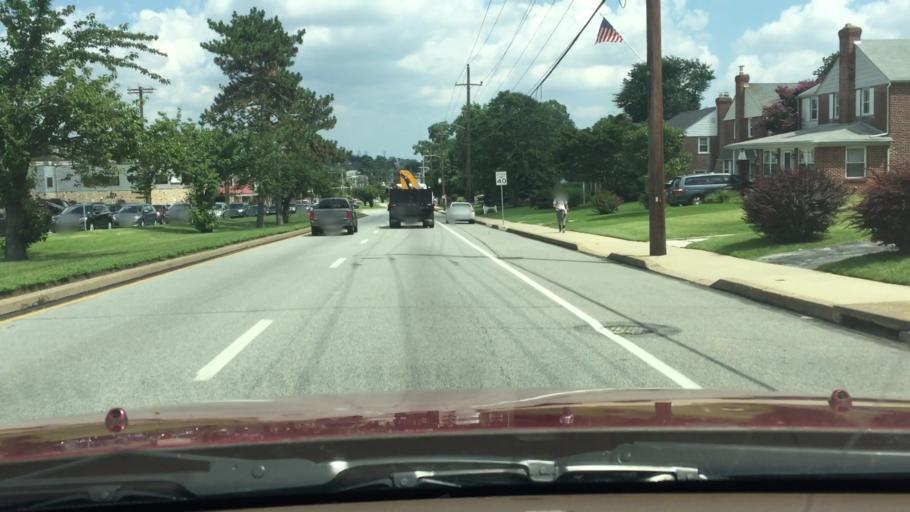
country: US
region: Pennsylvania
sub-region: Delaware County
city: Drexel Hill
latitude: 39.9709
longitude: -75.3080
